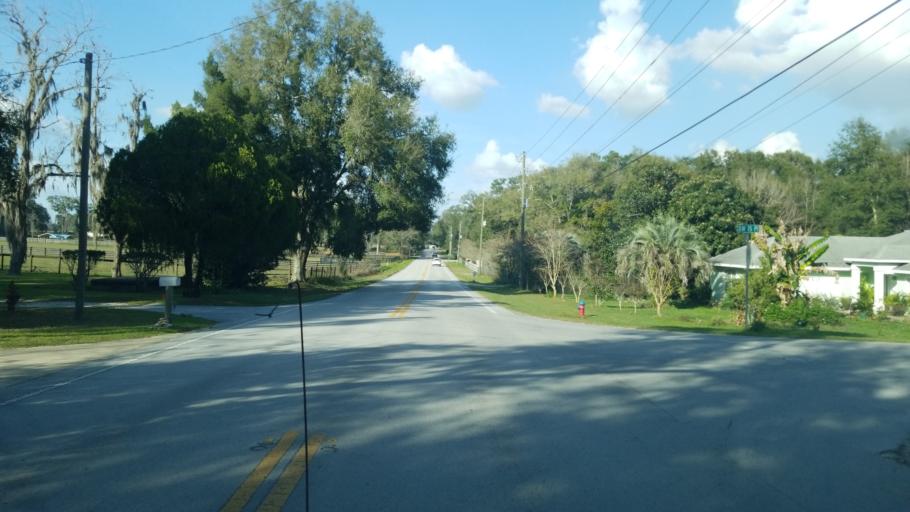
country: US
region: Florida
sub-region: Marion County
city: Ocala
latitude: 29.1719
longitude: -82.2518
